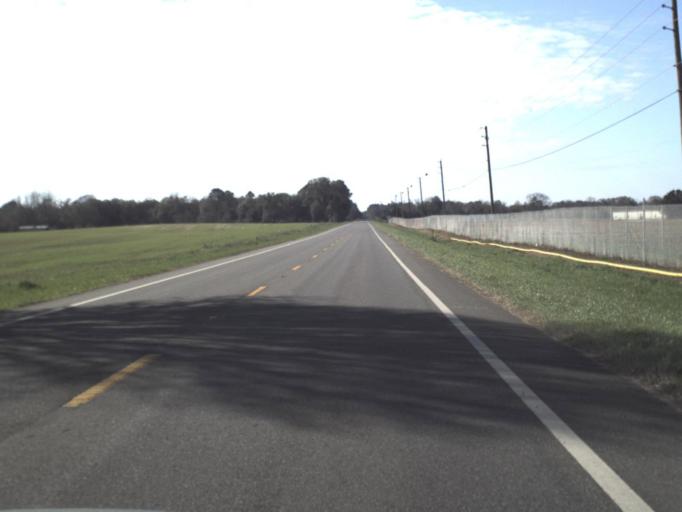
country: US
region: Florida
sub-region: Jackson County
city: Marianna
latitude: 30.8457
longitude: -85.1654
